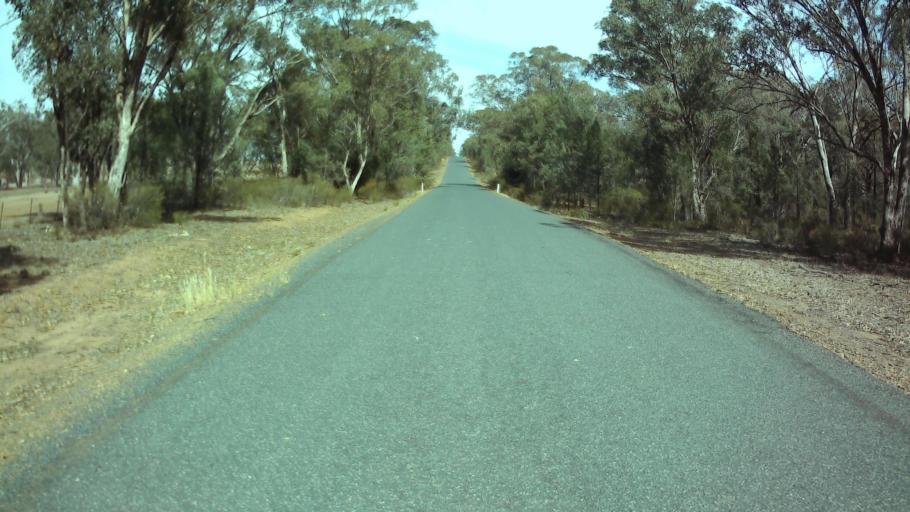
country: AU
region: New South Wales
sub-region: Weddin
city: Grenfell
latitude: -33.8070
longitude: 148.0523
